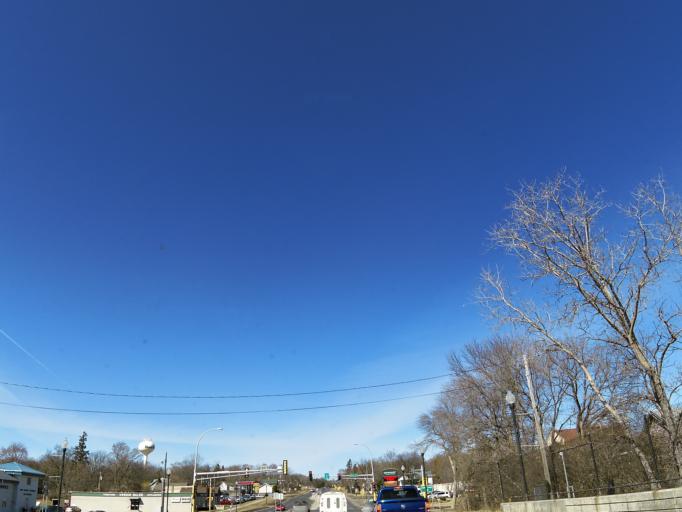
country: US
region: Minnesota
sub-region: Wright County
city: Rockford
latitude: 45.0866
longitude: -93.7350
